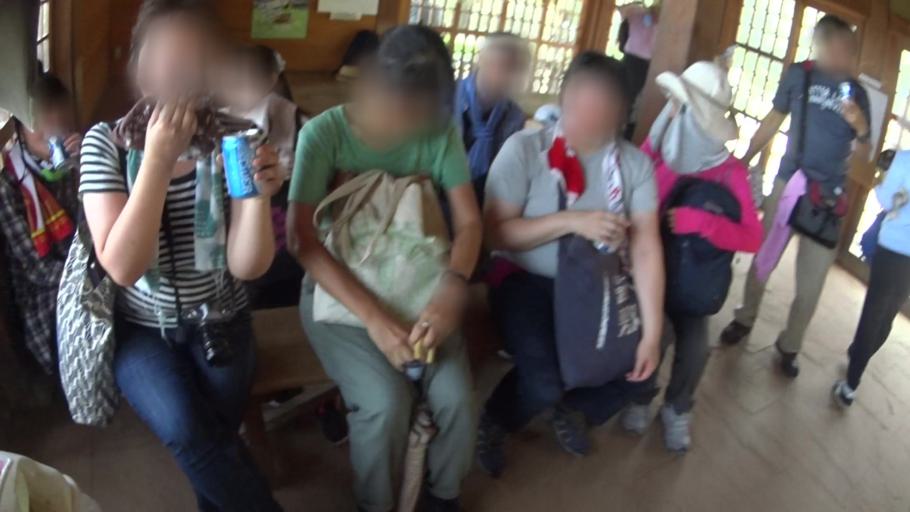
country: JP
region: Gunma
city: Ota
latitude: 36.3162
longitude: 139.3774
